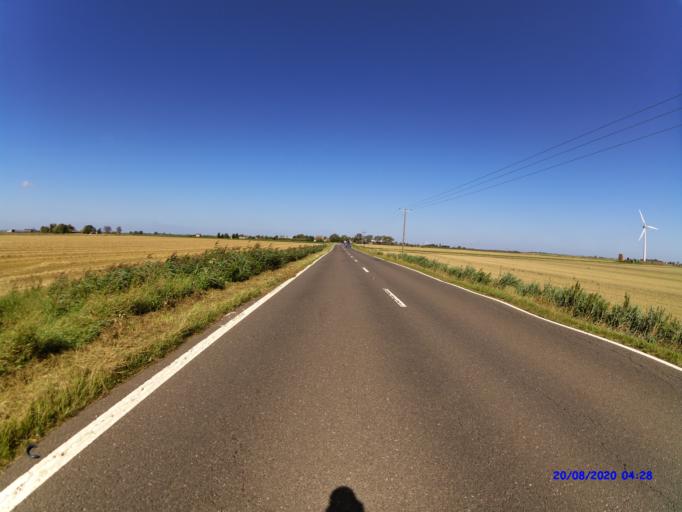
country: GB
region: England
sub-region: Cambridgeshire
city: Whittlesey
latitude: 52.5051
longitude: -0.1353
